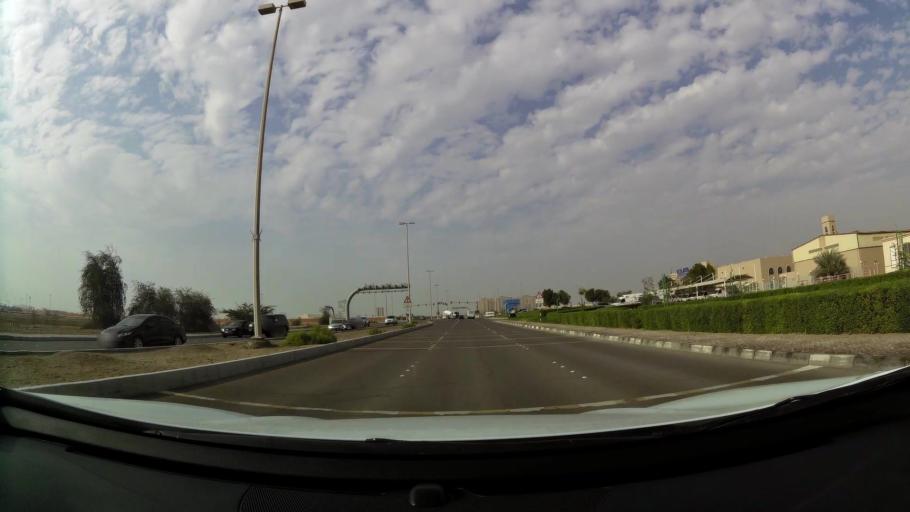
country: AE
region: Abu Dhabi
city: Abu Dhabi
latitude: 24.3593
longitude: 54.5373
